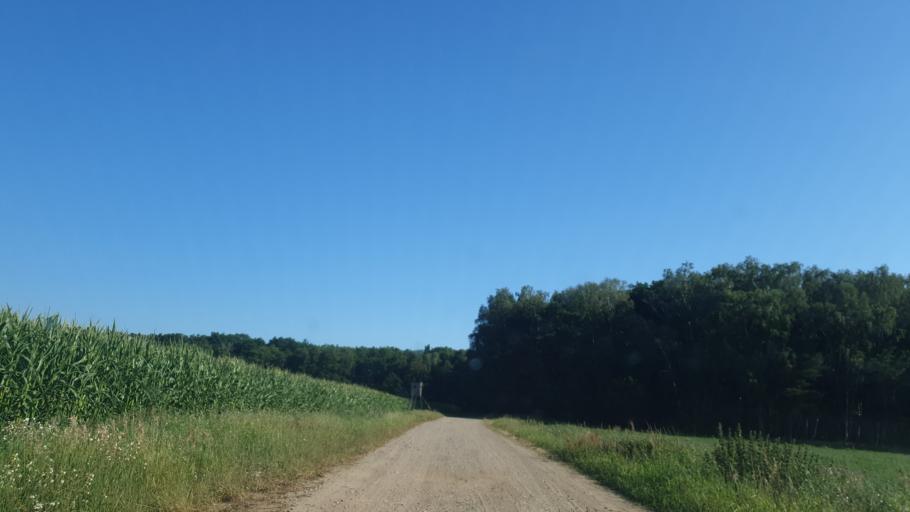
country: DE
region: Mecklenburg-Vorpommern
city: Torgelow
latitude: 53.6512
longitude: 13.9519
